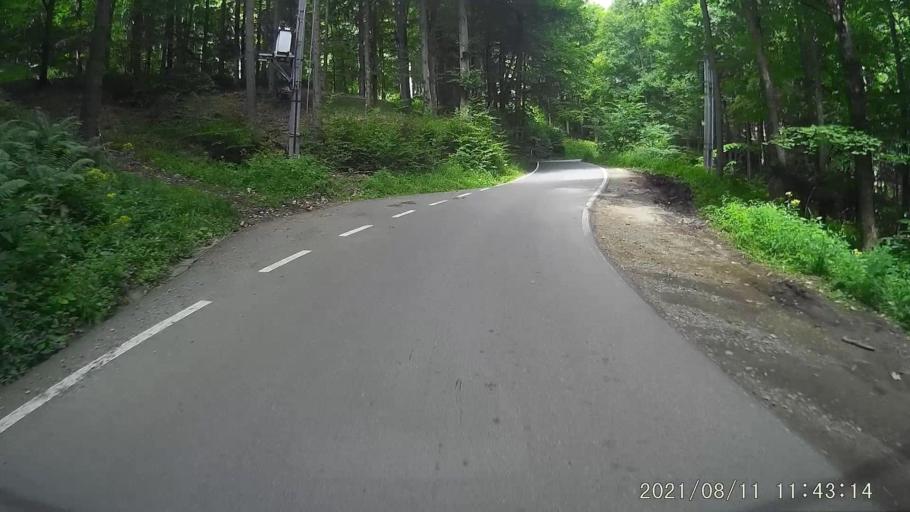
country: PL
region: Lower Silesian Voivodeship
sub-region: Powiat klodzki
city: Stronie Slaskie
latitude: 50.2486
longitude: 16.8439
